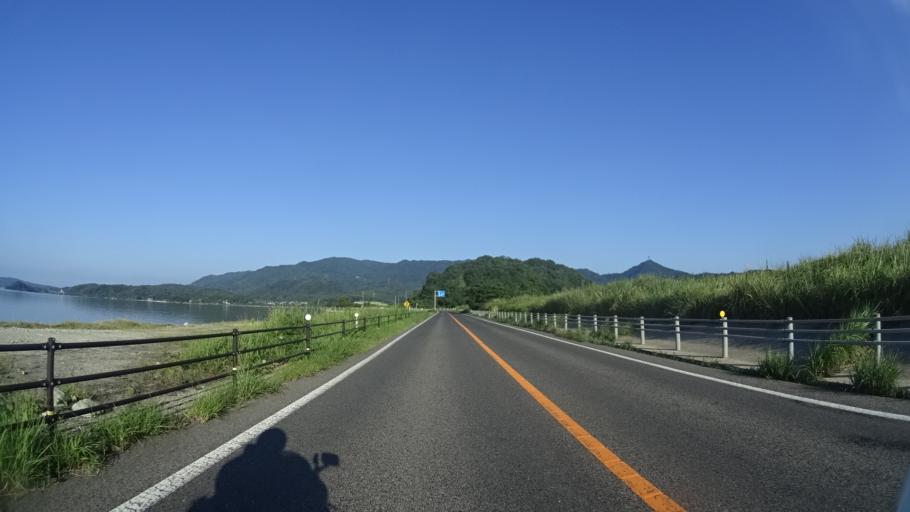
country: JP
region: Shimane
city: Sakaiminato
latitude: 35.5300
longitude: 133.1663
